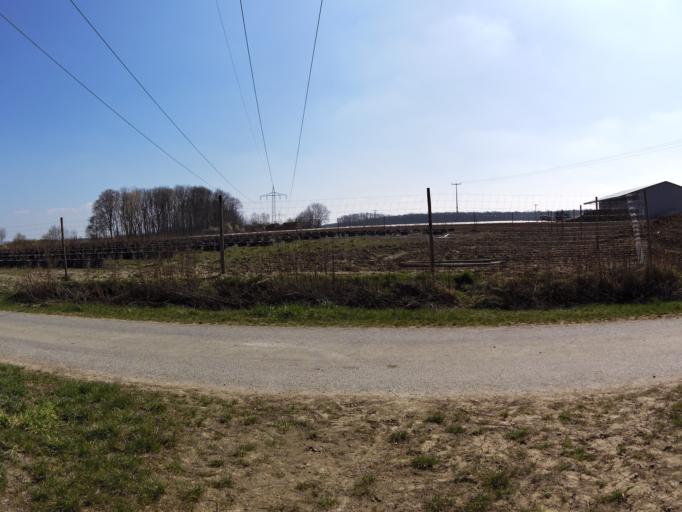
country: DE
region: Bavaria
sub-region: Regierungsbezirk Unterfranken
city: Biebelried
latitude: 49.7314
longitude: 10.0956
